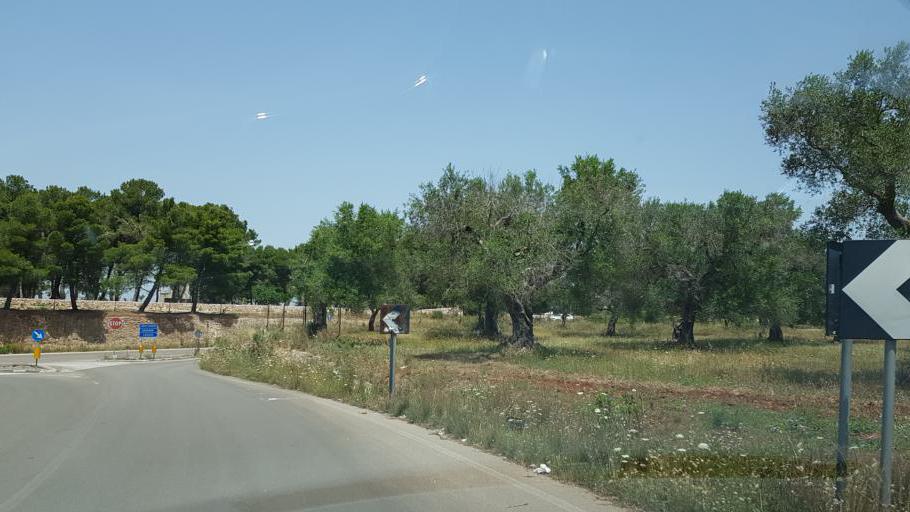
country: IT
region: Apulia
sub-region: Provincia di Lecce
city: Porto Cesareo
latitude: 40.2674
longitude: 17.9125
